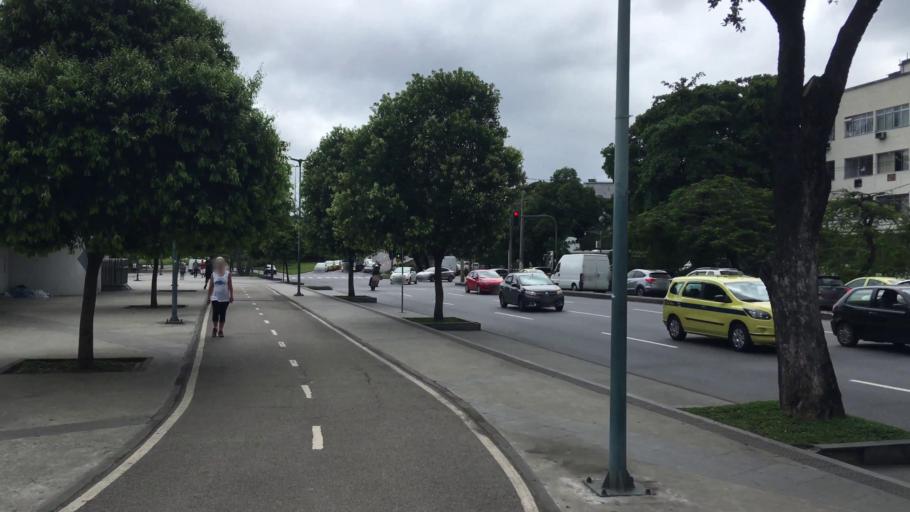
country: BR
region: Rio de Janeiro
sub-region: Rio De Janeiro
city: Rio de Janeiro
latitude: -22.9129
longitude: -43.2272
